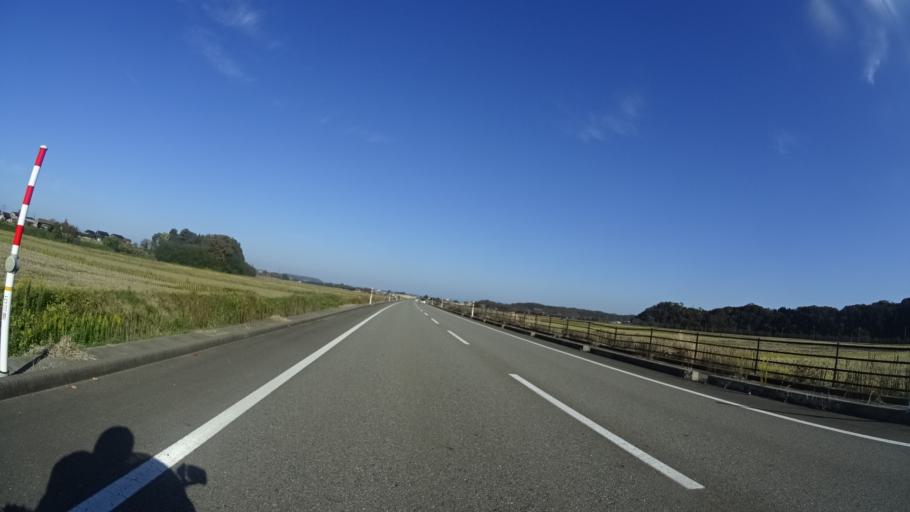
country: JP
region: Ishikawa
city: Komatsu
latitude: 36.2926
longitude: 136.3890
